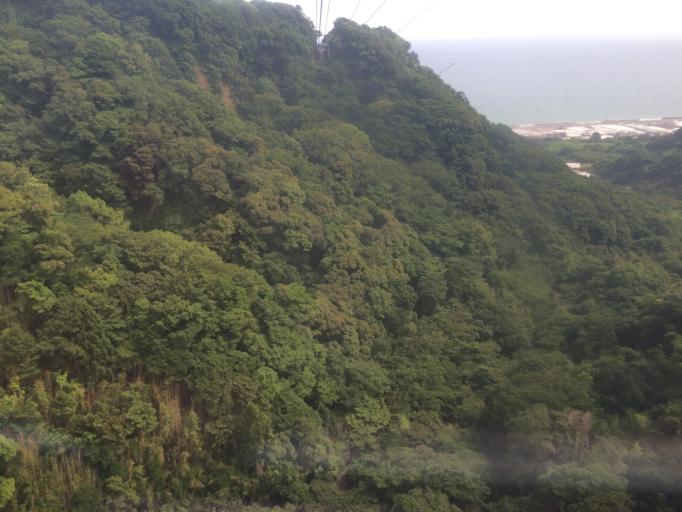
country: JP
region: Shizuoka
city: Shizuoka-shi
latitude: 34.9675
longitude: 138.4656
